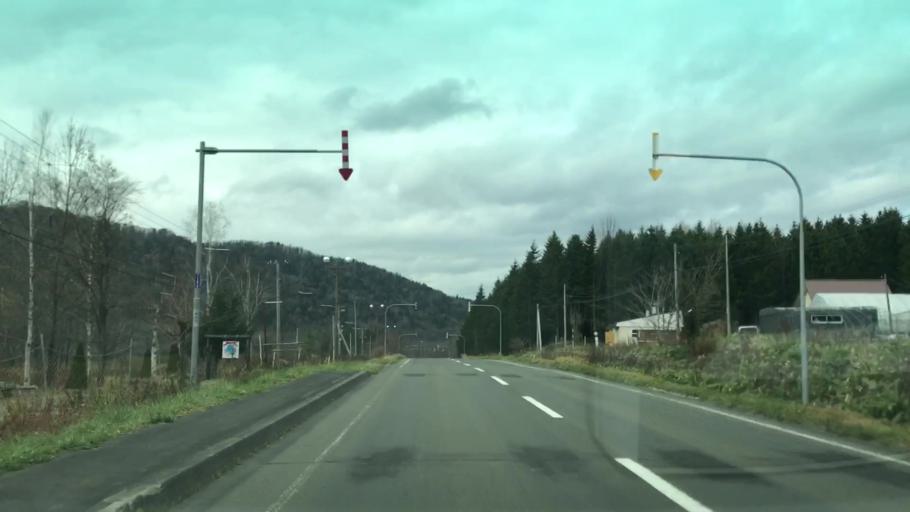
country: JP
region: Hokkaido
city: Shimo-furano
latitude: 42.9532
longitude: 142.4353
